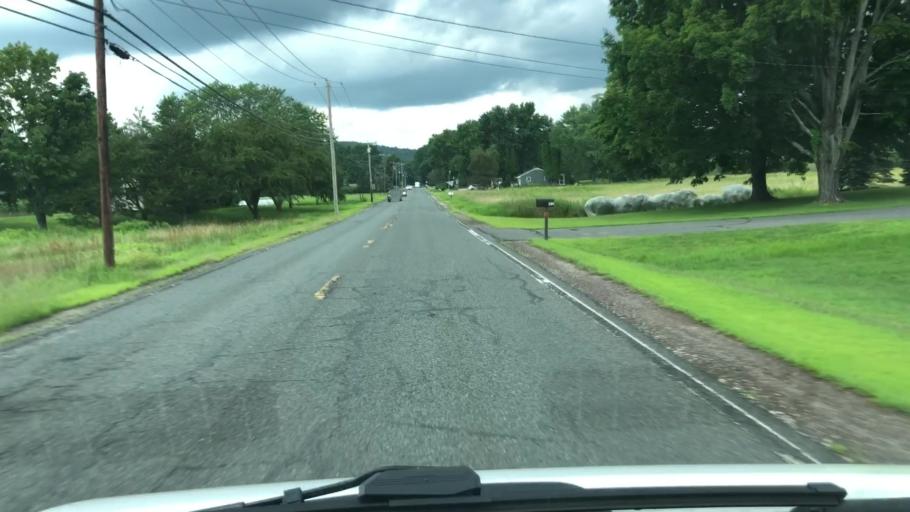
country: US
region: Massachusetts
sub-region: Franklin County
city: South Deerfield
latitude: 42.4883
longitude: -72.6251
